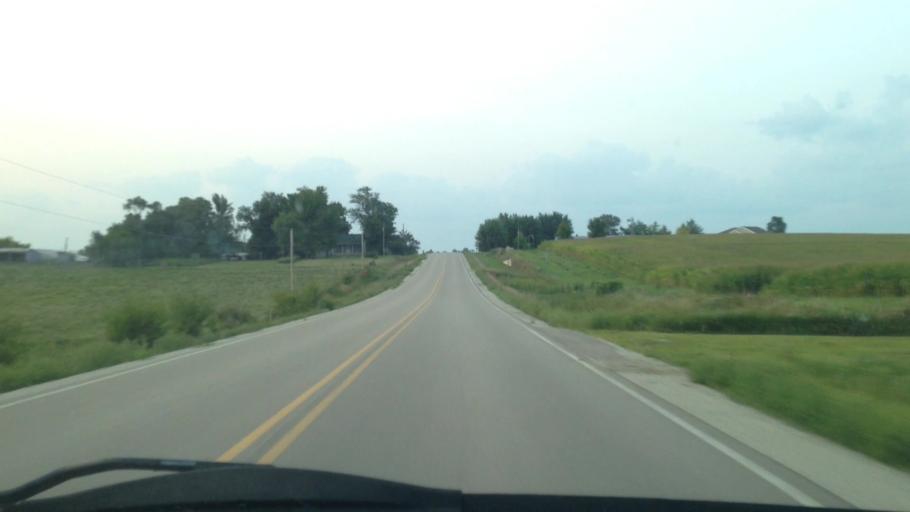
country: US
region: Iowa
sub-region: Benton County
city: Urbana
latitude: 42.2080
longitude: -91.8716
